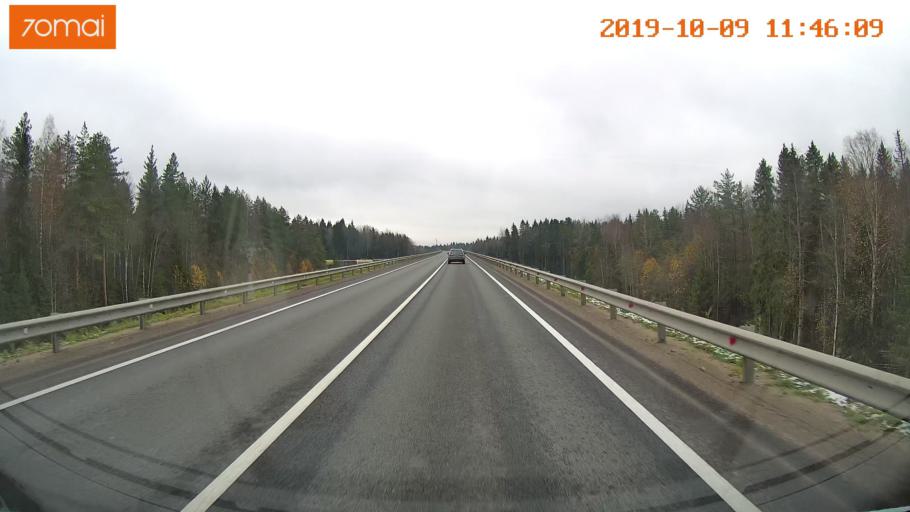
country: RU
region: Vologda
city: Gryazovets
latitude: 58.8581
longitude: 40.1998
